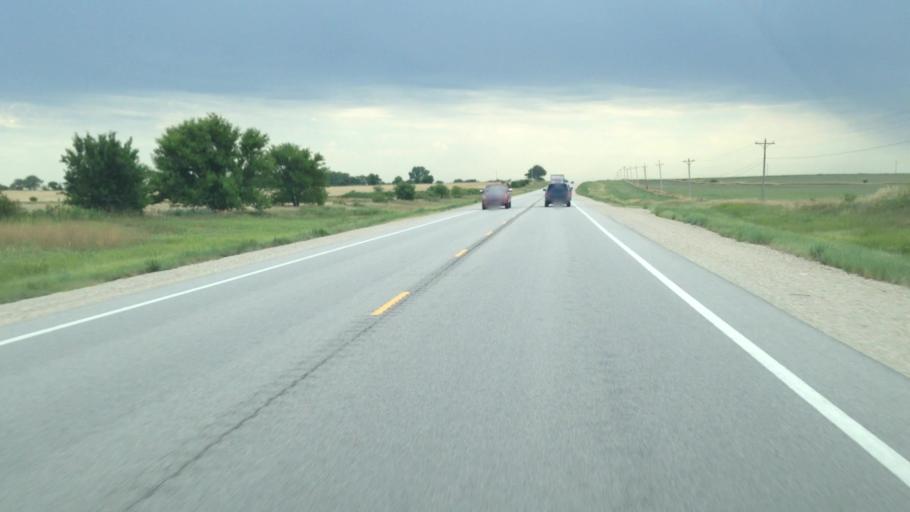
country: US
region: Kansas
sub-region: Coffey County
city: Burlington
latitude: 38.3386
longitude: -95.7292
